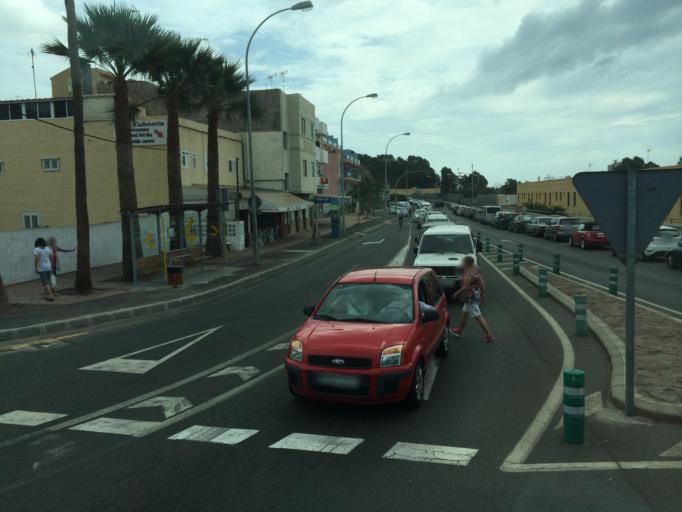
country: ES
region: Canary Islands
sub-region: Provincia de Las Palmas
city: Puerto Rico
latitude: 27.7583
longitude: -15.6798
